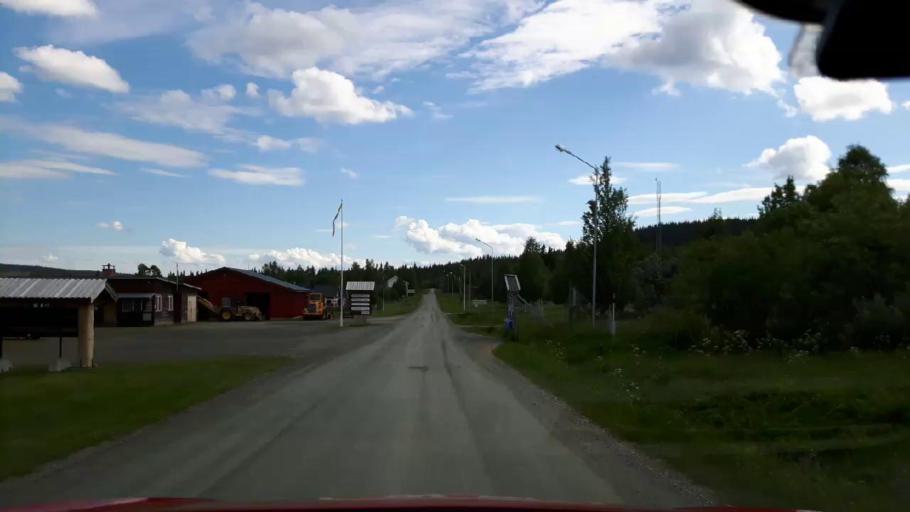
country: SE
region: Jaemtland
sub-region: Krokoms Kommun
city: Valla
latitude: 63.8274
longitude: 14.0406
